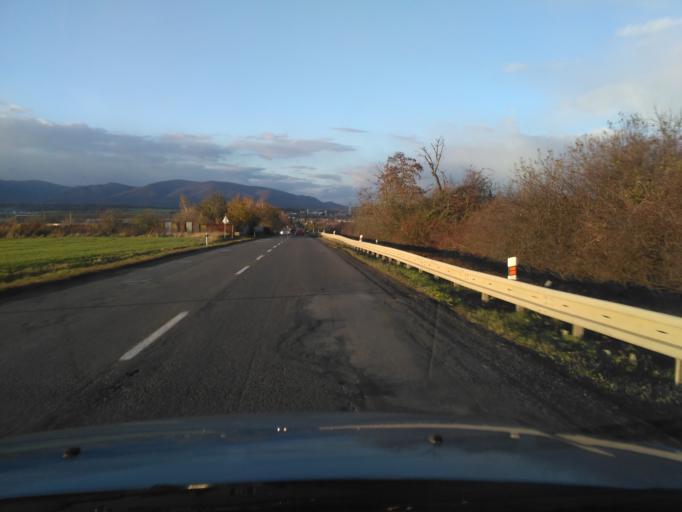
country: SK
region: Kosicky
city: Secovce
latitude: 48.6849
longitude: 21.6554
